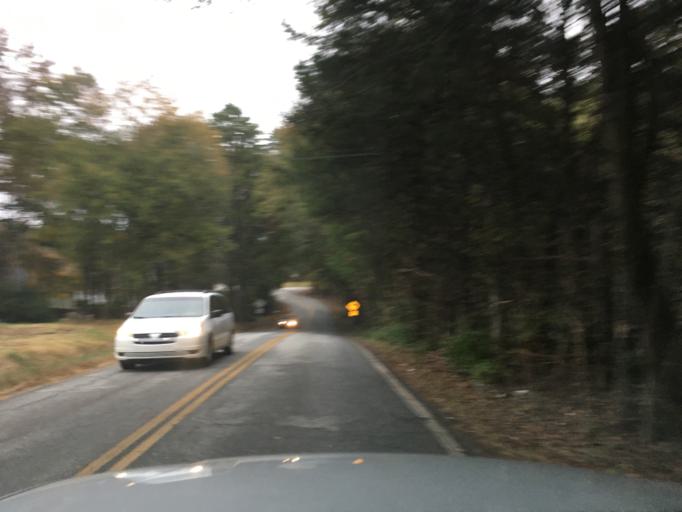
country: US
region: South Carolina
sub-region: Greenville County
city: Five Forks
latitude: 34.8285
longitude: -82.2710
